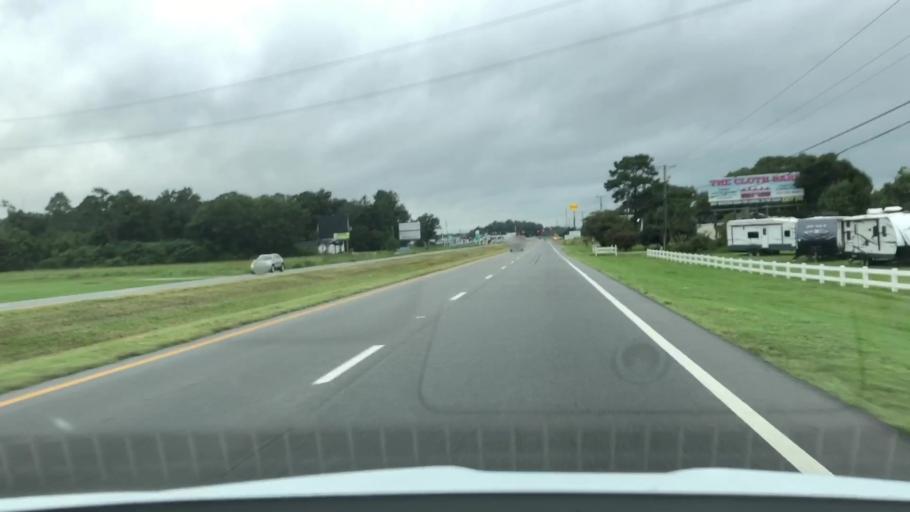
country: US
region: North Carolina
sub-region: Lenoir County
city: La Grange
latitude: 35.2828
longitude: -77.7533
